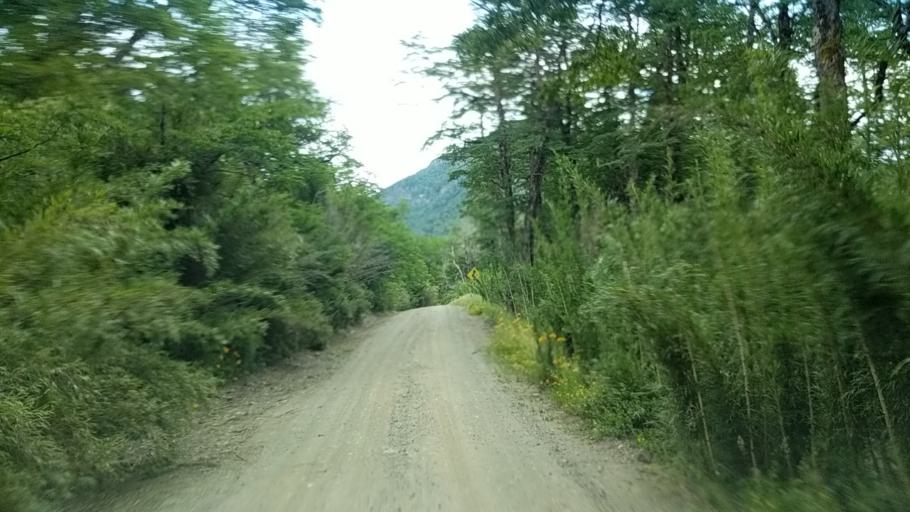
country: AR
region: Neuquen
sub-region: Departamento de Lacar
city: San Martin de los Andes
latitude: -39.8259
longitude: -71.6405
